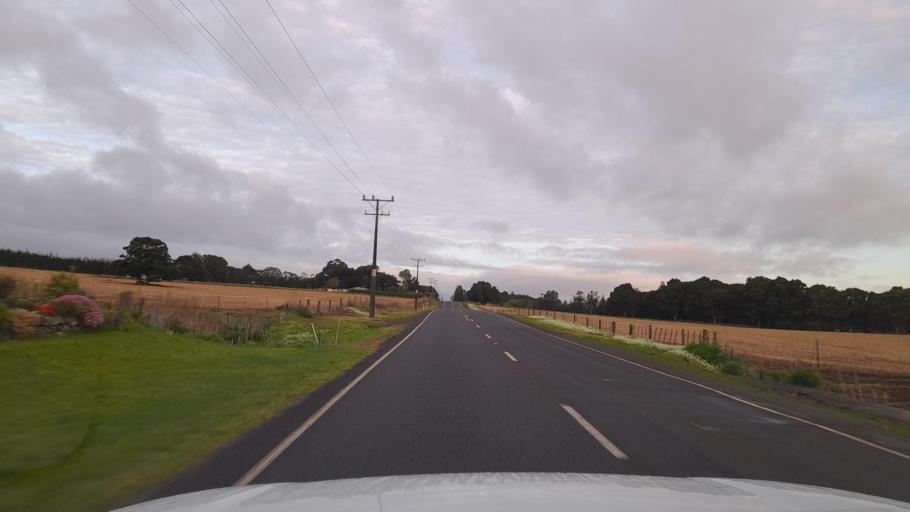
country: NZ
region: Northland
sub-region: Whangarei
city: Maungatapere
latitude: -35.7515
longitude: 174.1688
